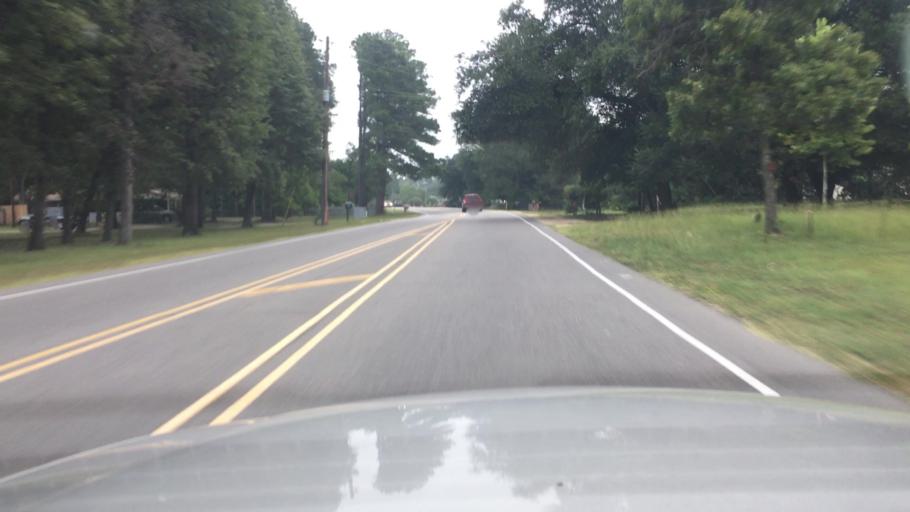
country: US
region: North Carolina
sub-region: Cumberland County
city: Hope Mills
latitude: 34.9754
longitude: -78.9958
